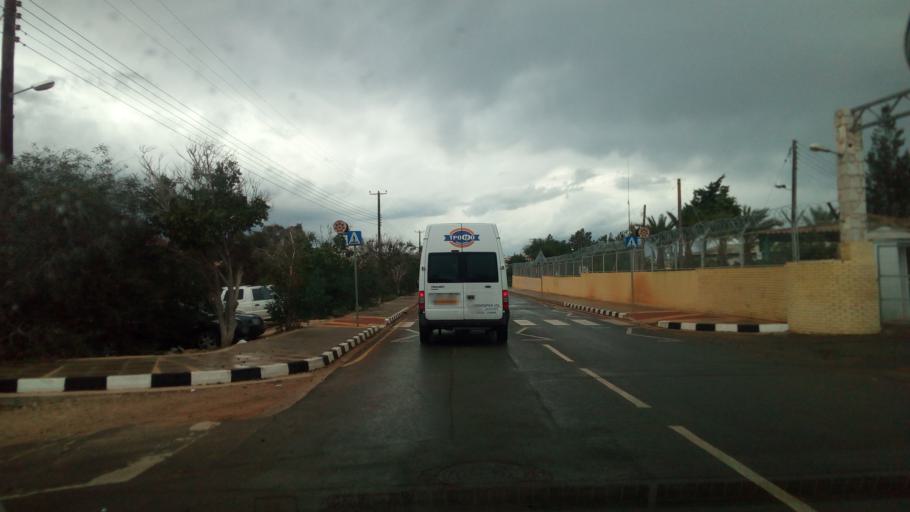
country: CY
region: Ammochostos
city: Liopetri
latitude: 35.0033
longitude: 33.8931
